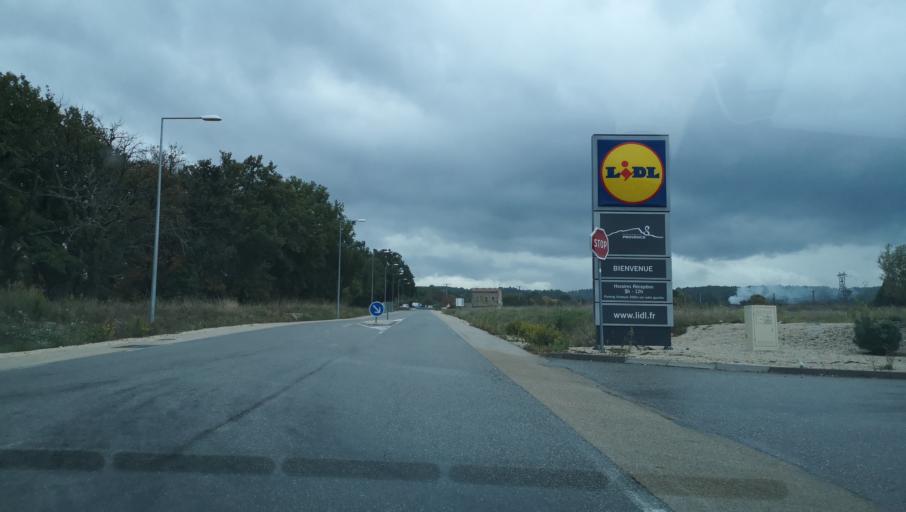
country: FR
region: Provence-Alpes-Cote d'Azur
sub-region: Departement des Bouches-du-Rhone
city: Rousset
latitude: 43.4733
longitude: 5.5939
